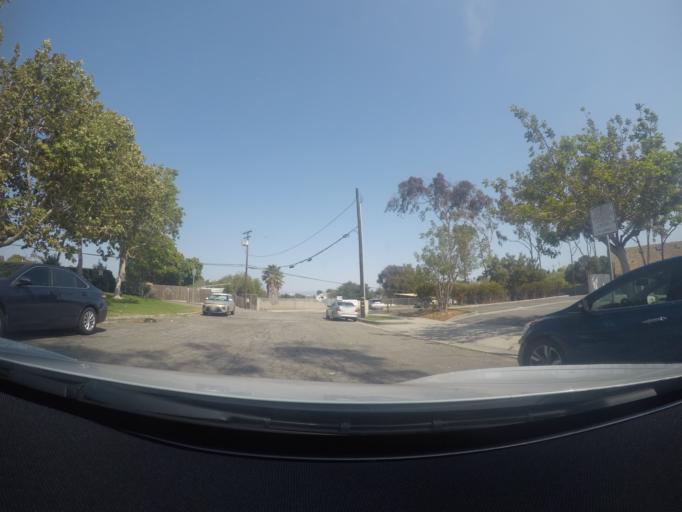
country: US
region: California
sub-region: Los Angeles County
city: Torrance
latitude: 33.8251
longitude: -118.3690
